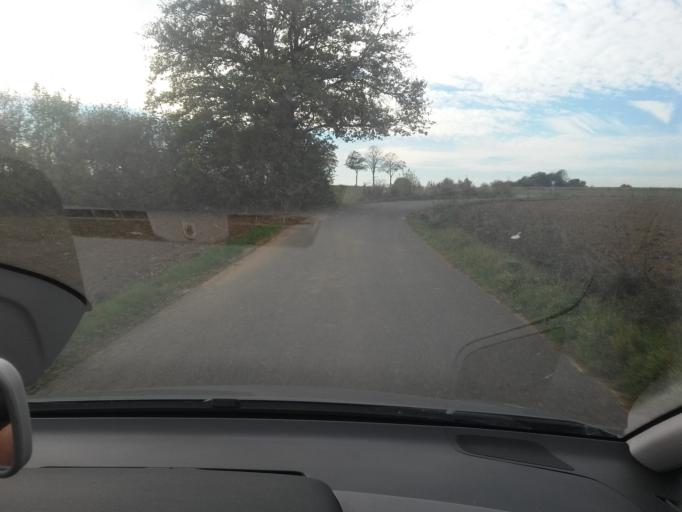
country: BE
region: Wallonia
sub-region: Province du Luxembourg
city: Attert
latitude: 49.7072
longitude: 5.7164
